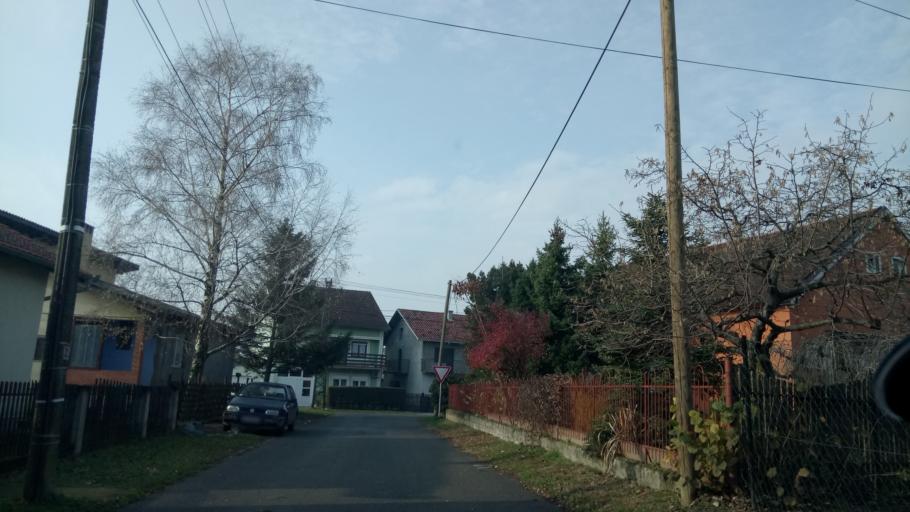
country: RS
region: Autonomna Pokrajina Vojvodina
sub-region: Sremski Okrug
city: Stara Pazova
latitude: 44.9820
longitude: 20.1730
